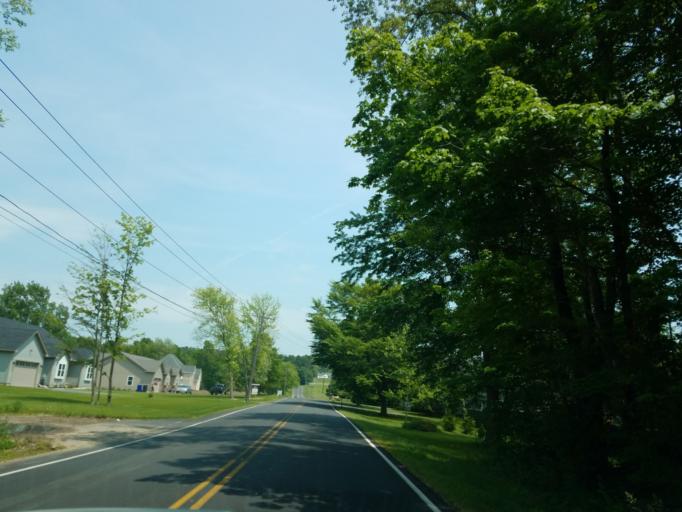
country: US
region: Connecticut
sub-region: Hartford County
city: Thompsonville
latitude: 42.0242
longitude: -72.6232
